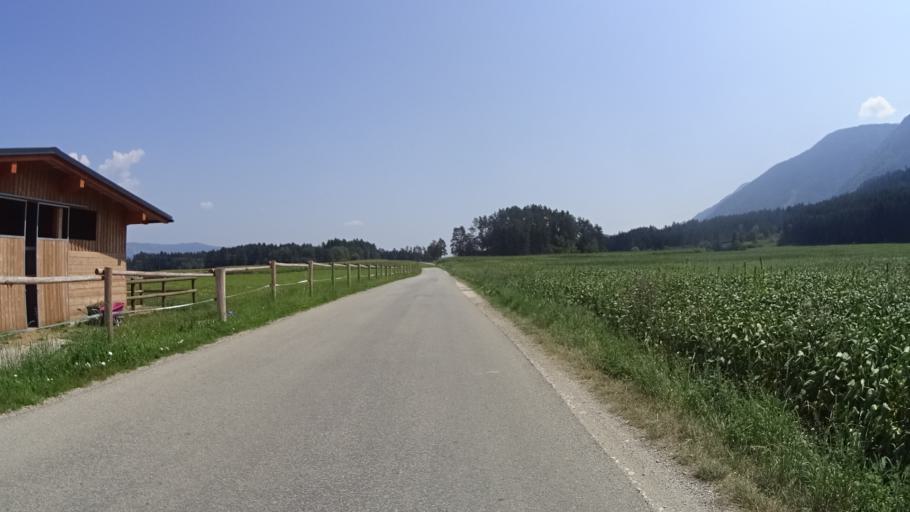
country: AT
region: Carinthia
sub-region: Politischer Bezirk Volkermarkt
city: Globasnitz
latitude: 46.5570
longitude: 14.7063
